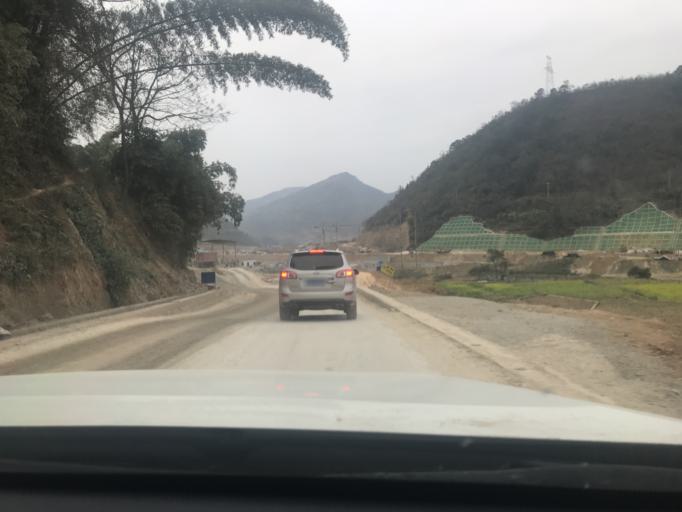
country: CN
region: Guangxi Zhuangzu Zizhiqu
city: Xinzhou
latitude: 25.0101
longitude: 105.8458
